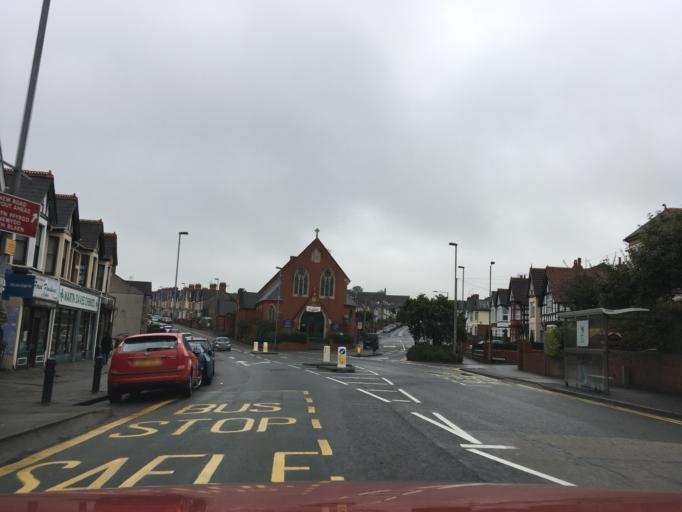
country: GB
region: Wales
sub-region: Newport
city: Newport
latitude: 51.5974
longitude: -2.9816
